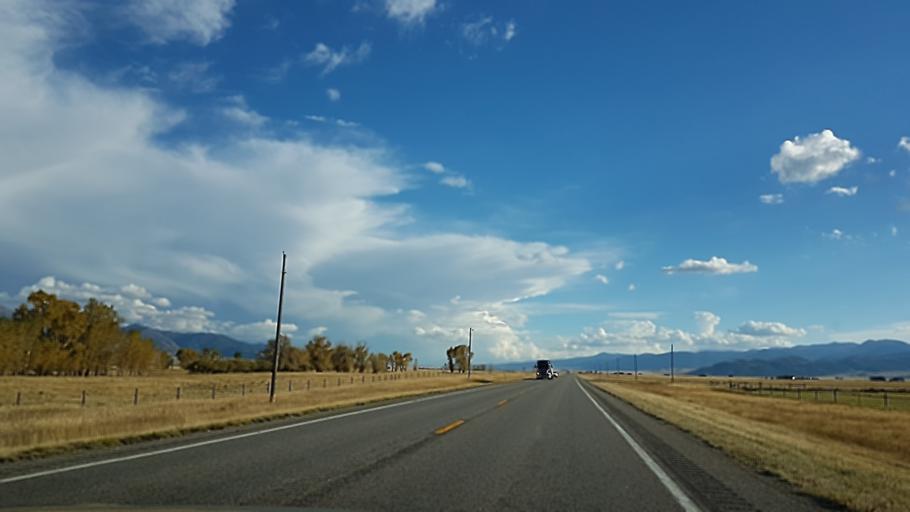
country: US
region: Montana
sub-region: Madison County
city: Virginia City
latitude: 45.1975
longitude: -111.6788
